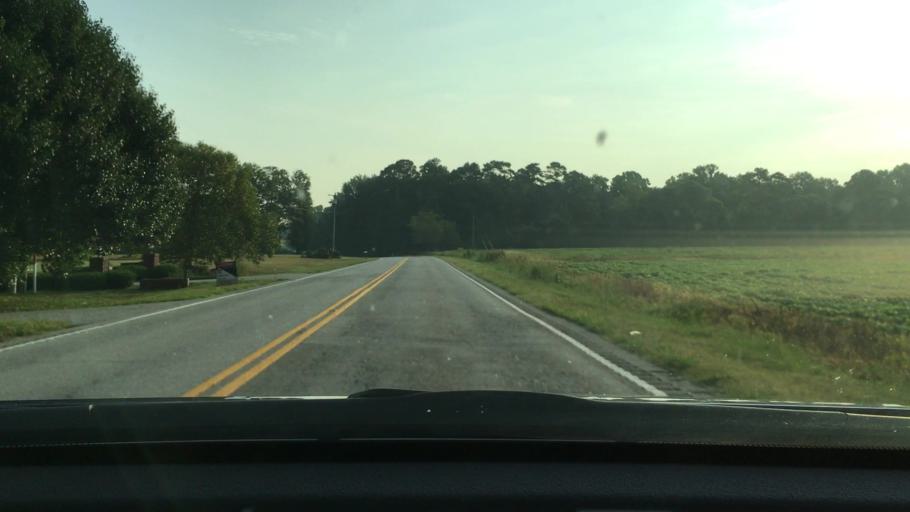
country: US
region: South Carolina
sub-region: Florence County
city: Timmonsville
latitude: 34.1883
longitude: -80.0449
